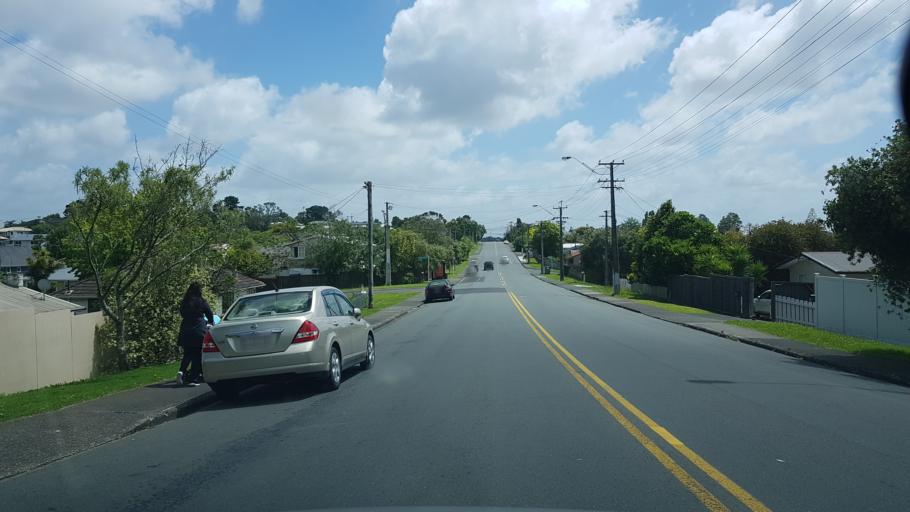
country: NZ
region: Auckland
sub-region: Auckland
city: North Shore
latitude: -36.8024
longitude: 174.6914
